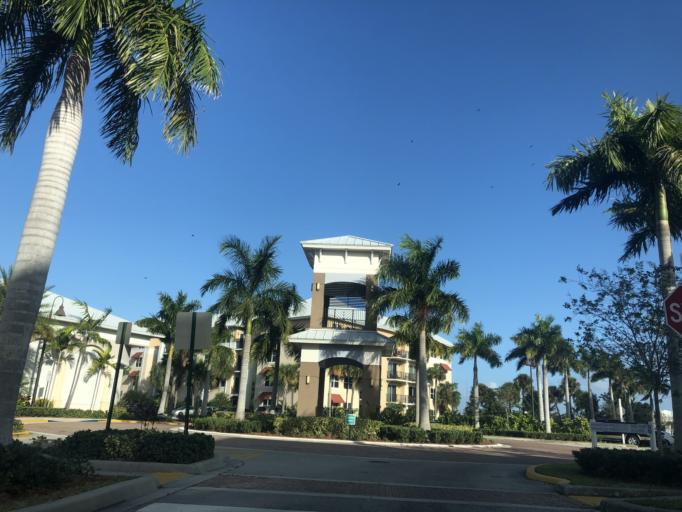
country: US
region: Florida
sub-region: Palm Beach County
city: West Palm Beach
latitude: 26.7196
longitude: -80.0789
